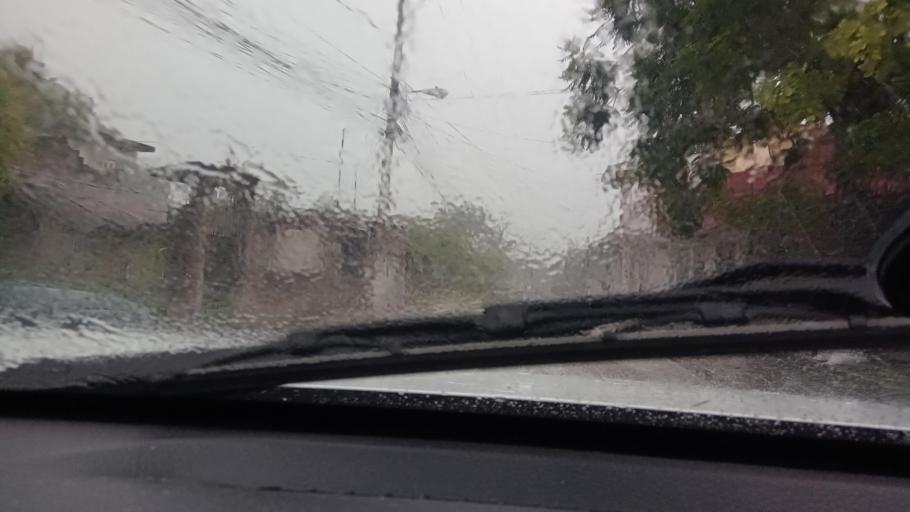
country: MX
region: Veracruz
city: Coatepec
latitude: 19.4591
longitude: -96.9755
